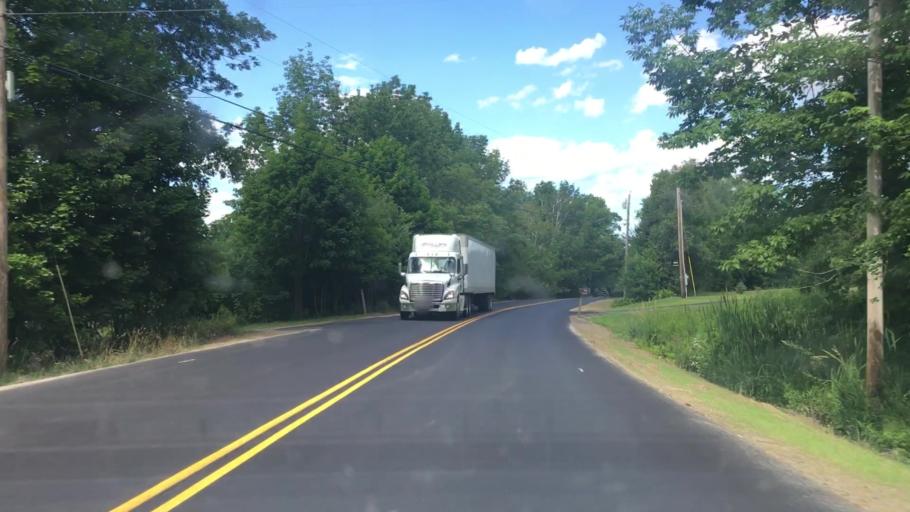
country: US
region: Maine
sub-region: Franklin County
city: Wilton
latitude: 44.5547
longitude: -70.1835
